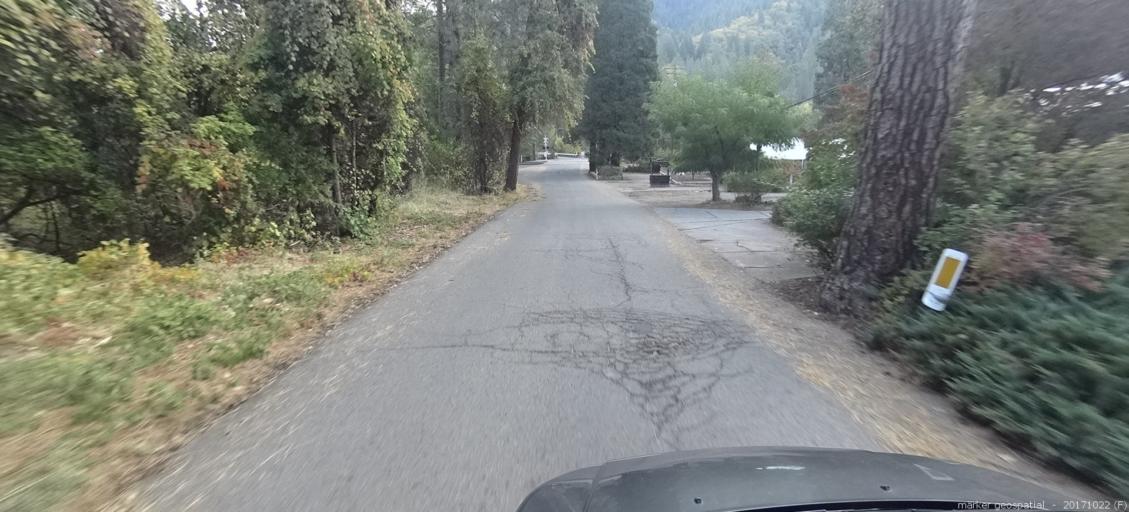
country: US
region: California
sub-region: Siskiyou County
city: Dunsmuir
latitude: 41.1836
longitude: -122.2861
